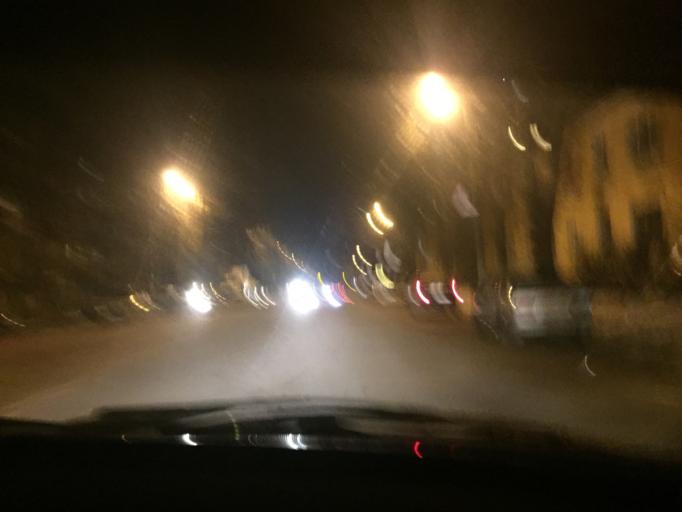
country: RU
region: Tula
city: Mendeleyevskiy
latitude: 54.1643
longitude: 37.5941
